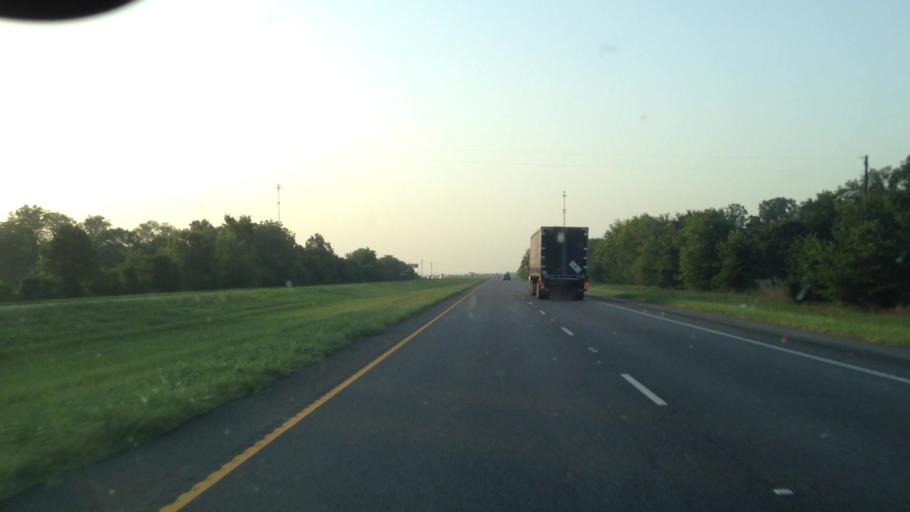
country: US
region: Louisiana
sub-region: Red River Parish
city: Coushatta
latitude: 31.8473
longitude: -93.2964
